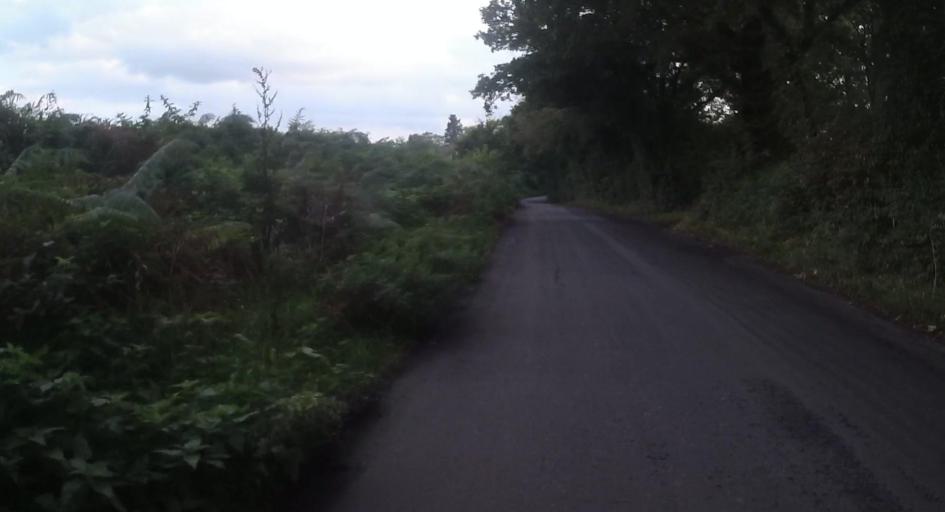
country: GB
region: England
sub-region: West Berkshire
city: Thatcham
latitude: 51.4057
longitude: -1.1872
